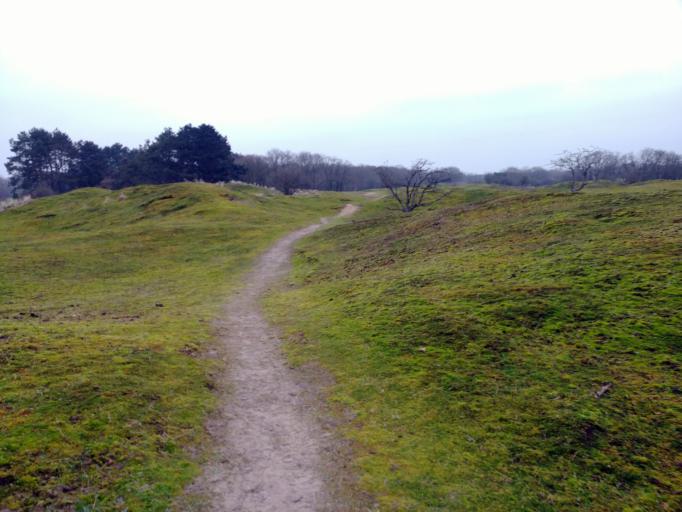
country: NL
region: South Holland
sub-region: Gemeente Hillegom
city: Hillegom
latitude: 52.3094
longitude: 4.5373
